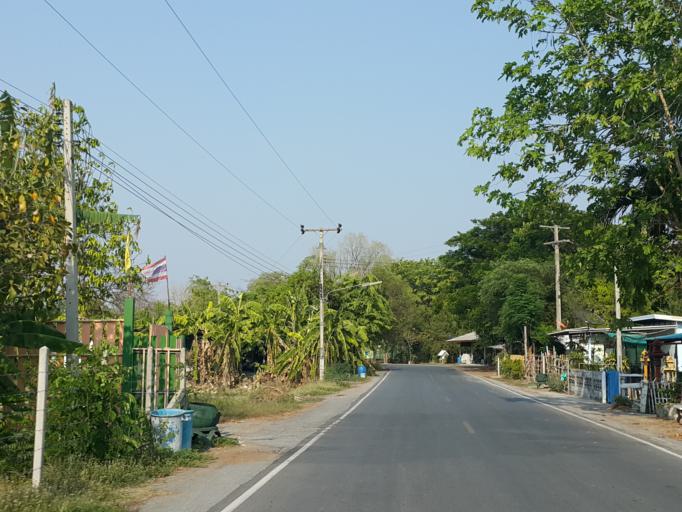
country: TH
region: Suphan Buri
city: Sam Chuk
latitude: 14.7469
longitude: 100.0501
